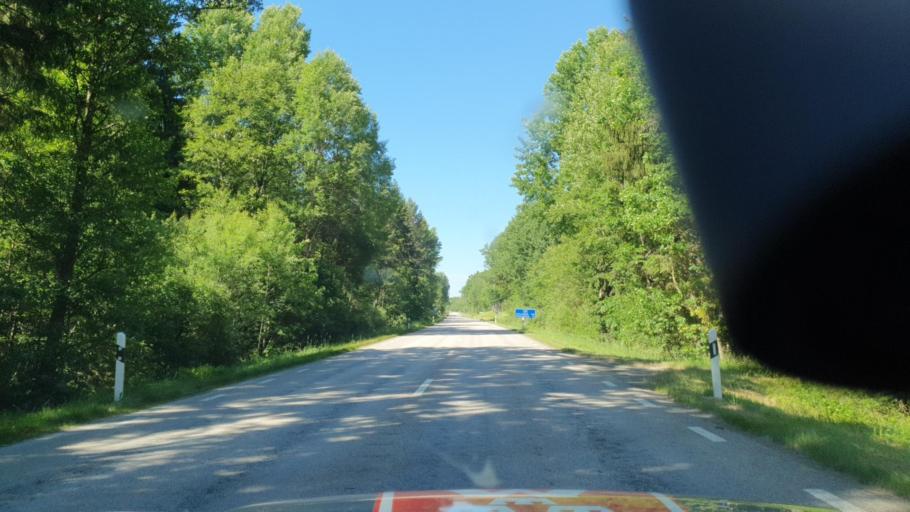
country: SE
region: Kalmar
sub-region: Emmaboda Kommun
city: Emmaboda
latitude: 56.5397
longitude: 15.6130
